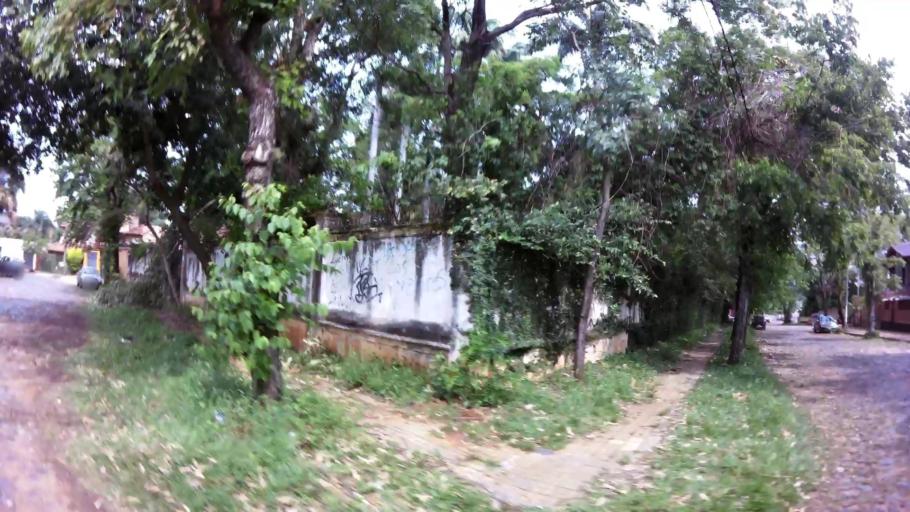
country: PY
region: Central
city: Fernando de la Mora
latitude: -25.2782
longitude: -57.5601
